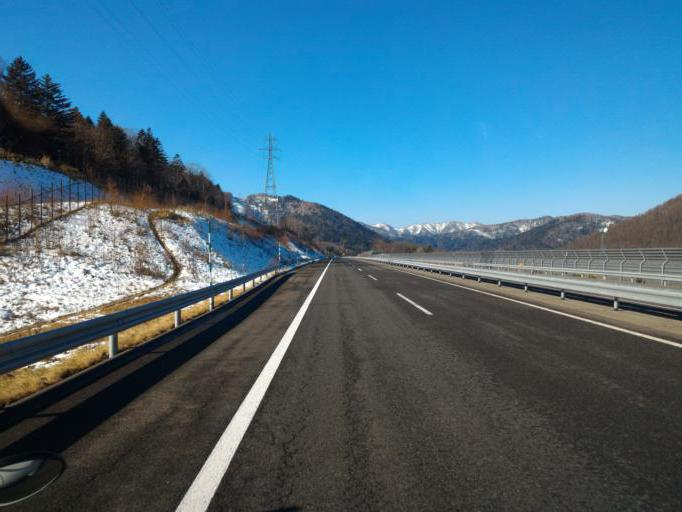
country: JP
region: Hokkaido
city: Shimo-furano
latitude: 43.0535
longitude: 142.5791
